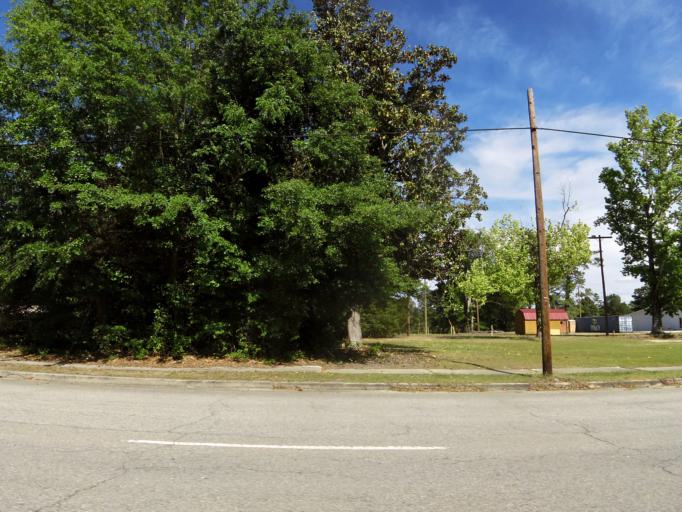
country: US
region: South Carolina
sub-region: Bamberg County
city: Denmark
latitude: 33.3010
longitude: -81.1454
